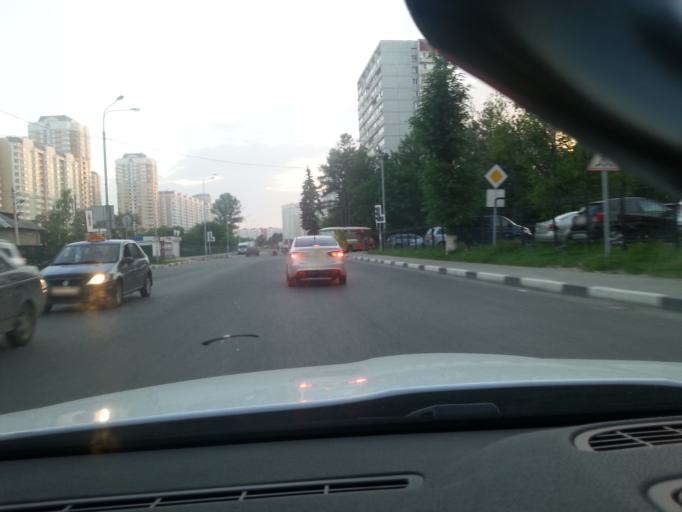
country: RU
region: Moskovskaya
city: Zheleznodorozhnyy
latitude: 55.7433
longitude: 38.0096
